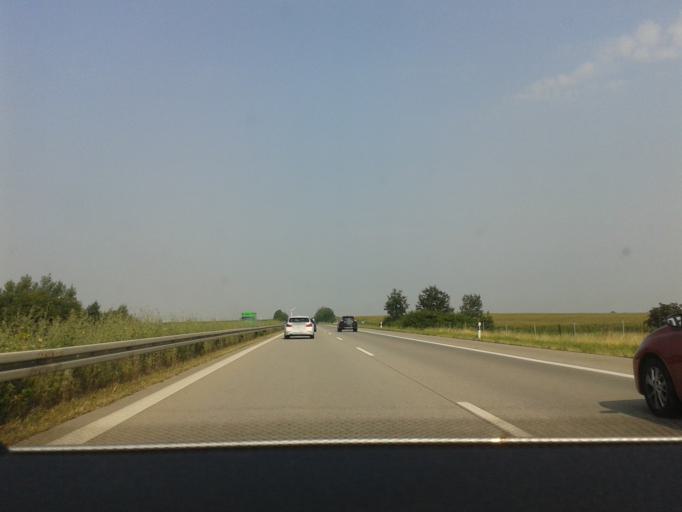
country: DE
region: Saxony
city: Grossweitzschen
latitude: 51.1756
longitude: 13.0348
